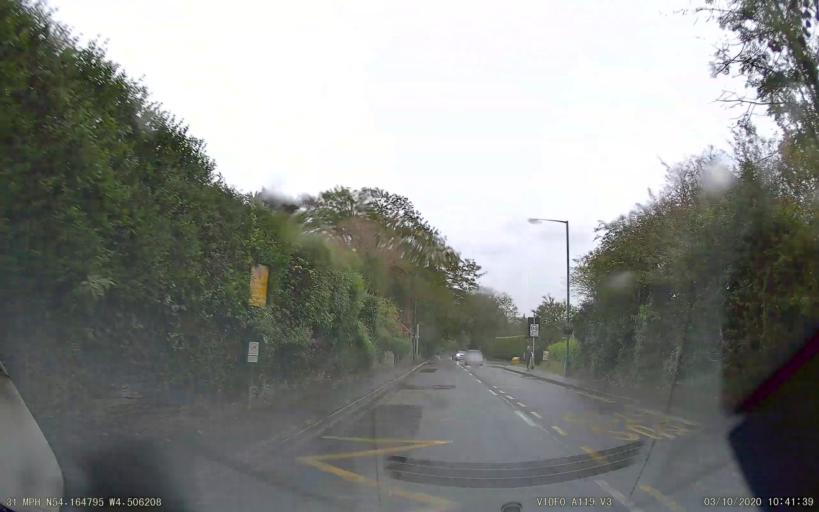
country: IM
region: Douglas
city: Douglas
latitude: 54.1648
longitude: -4.5062
